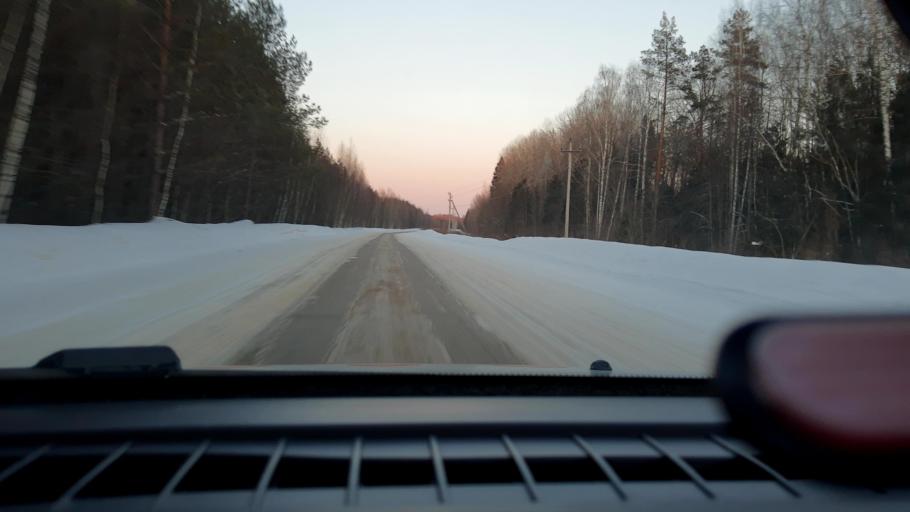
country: RU
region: Nizjnij Novgorod
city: Lyskovo
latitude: 56.1630
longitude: 45.2133
